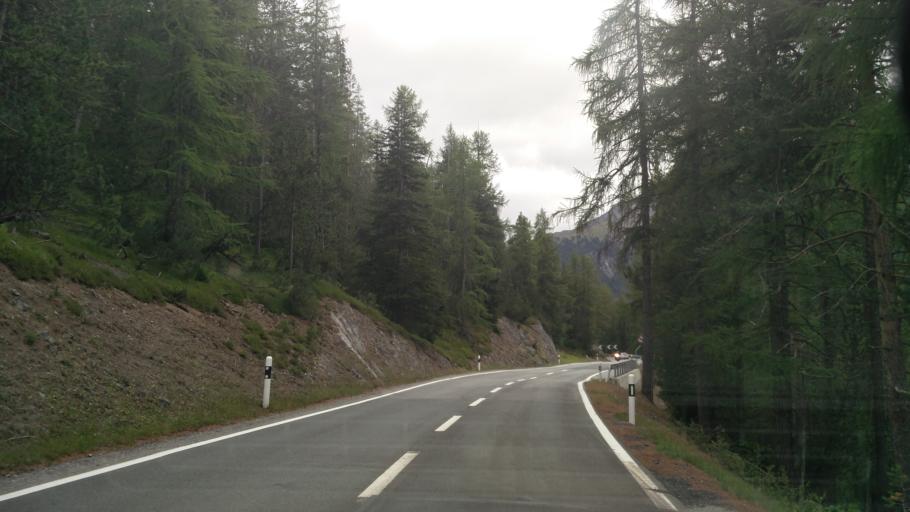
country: CH
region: Grisons
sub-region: Inn District
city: Zernez
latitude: 46.6642
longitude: 10.1692
